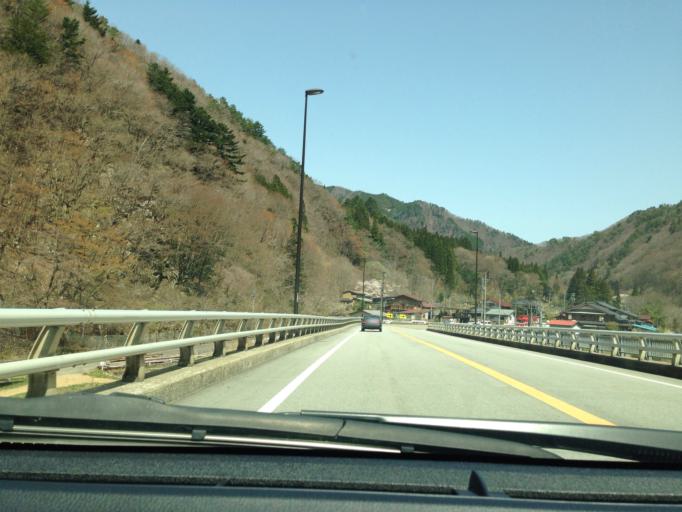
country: JP
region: Gifu
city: Takayama
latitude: 36.0074
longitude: 137.2919
